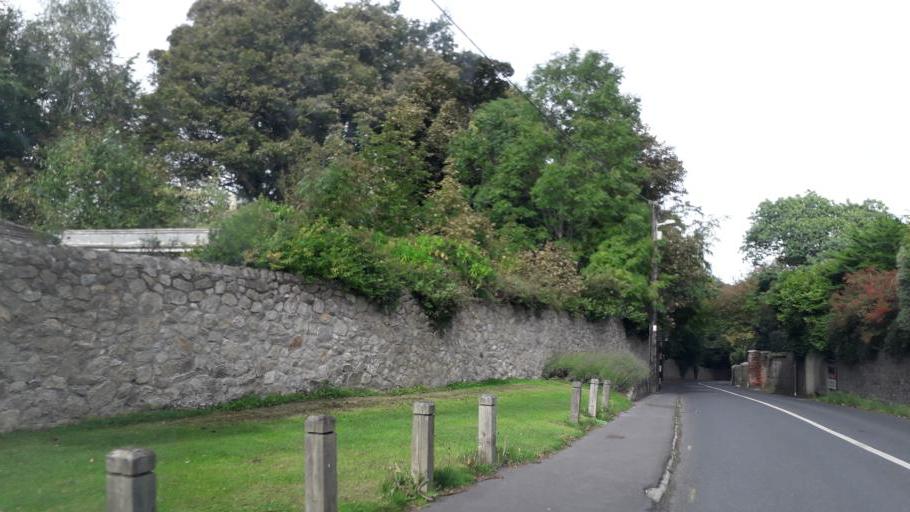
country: IE
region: Leinster
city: Cabinteely
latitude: 53.2582
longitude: -6.1526
